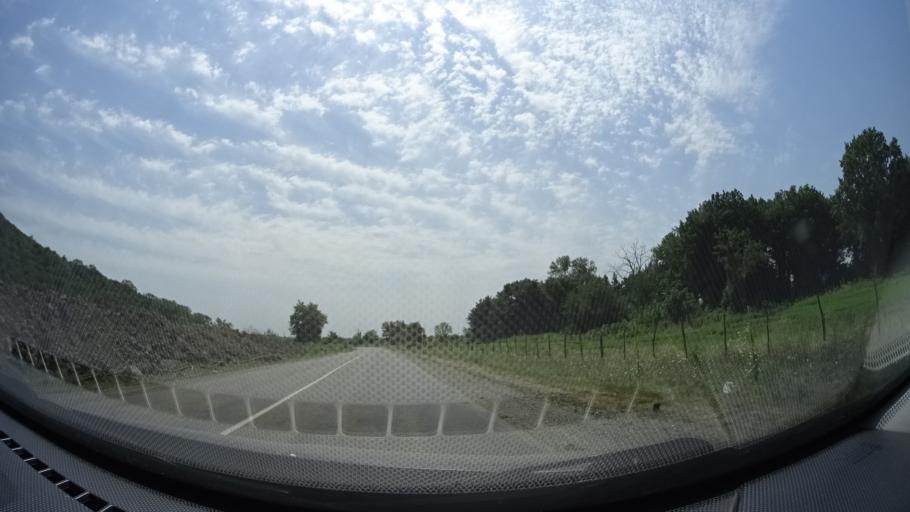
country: GE
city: Bagdadi
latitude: 41.8567
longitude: 46.0279
